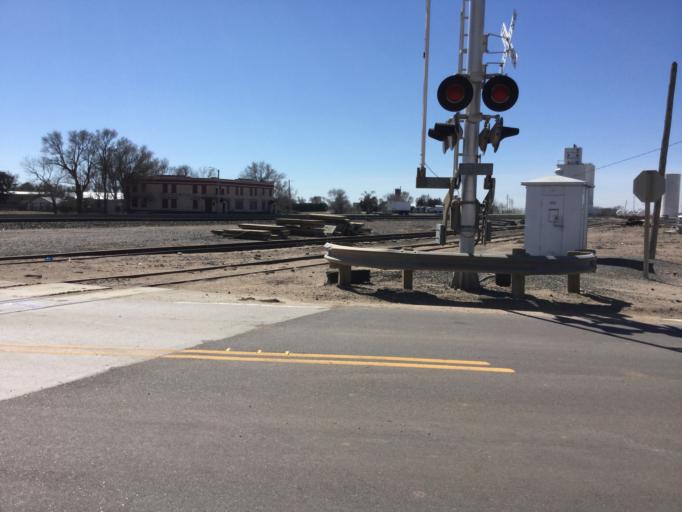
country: US
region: Kansas
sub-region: Barber County
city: Kiowa
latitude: 37.0171
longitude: -98.4920
